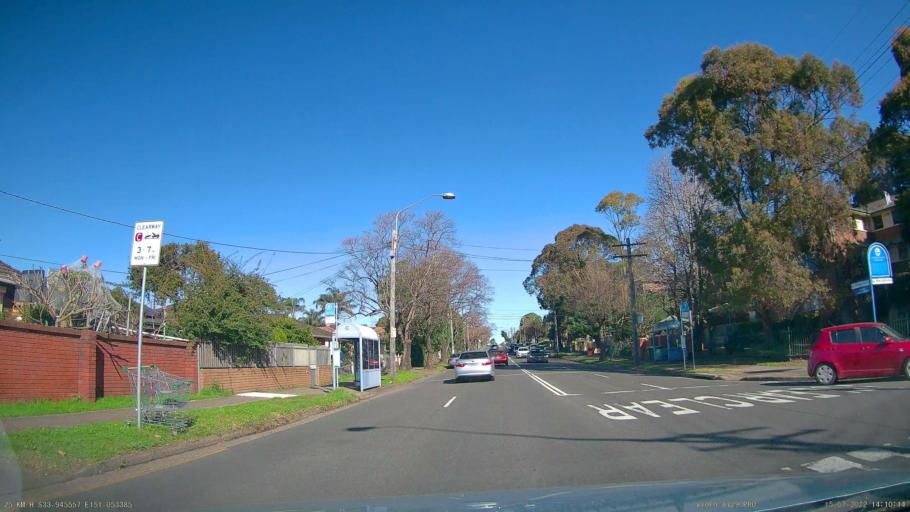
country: AU
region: New South Wales
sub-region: Hurstville
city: Peakhurst
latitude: -33.9457
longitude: 151.0534
